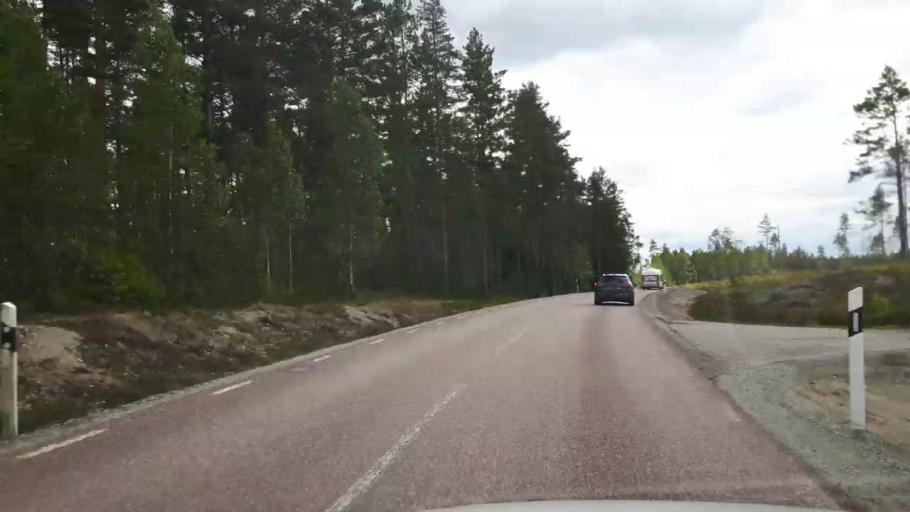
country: SE
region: Vaestmanland
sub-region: Skinnskattebergs Kommun
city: Skinnskatteberg
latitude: 59.8083
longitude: 15.8417
